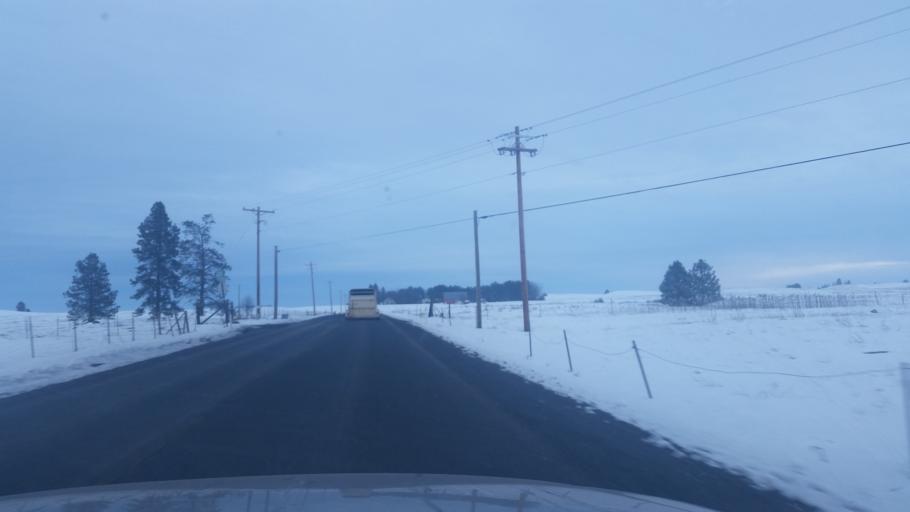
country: US
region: Washington
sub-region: Spokane County
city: Cheney
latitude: 47.5004
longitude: -117.6514
